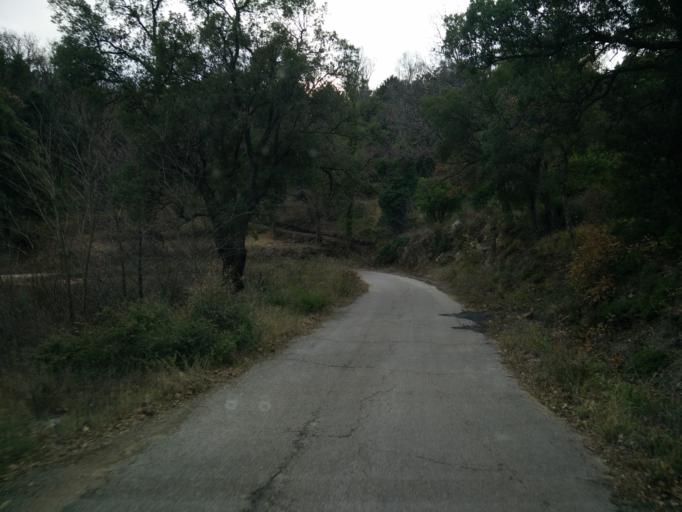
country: FR
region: Provence-Alpes-Cote d'Azur
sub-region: Departement du Var
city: Roquebrune-sur-Argens
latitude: 43.3841
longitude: 6.6116
